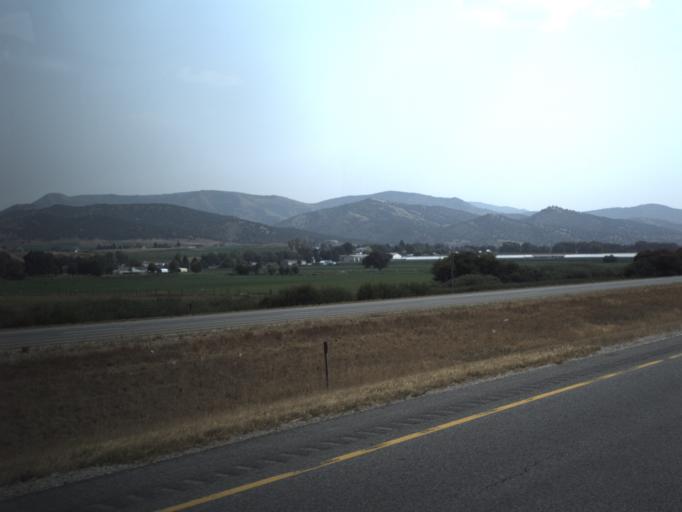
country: US
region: Utah
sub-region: Summit County
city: Coalville
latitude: 40.8906
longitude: -111.3943
